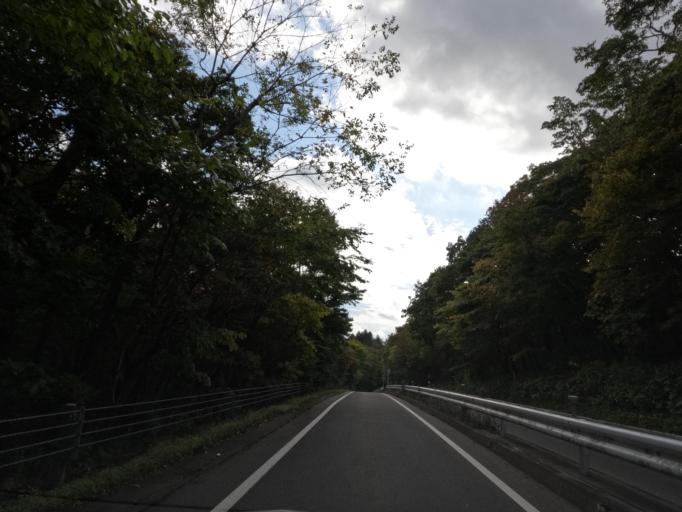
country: JP
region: Hokkaido
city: Chitose
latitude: 42.8067
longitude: 141.5849
